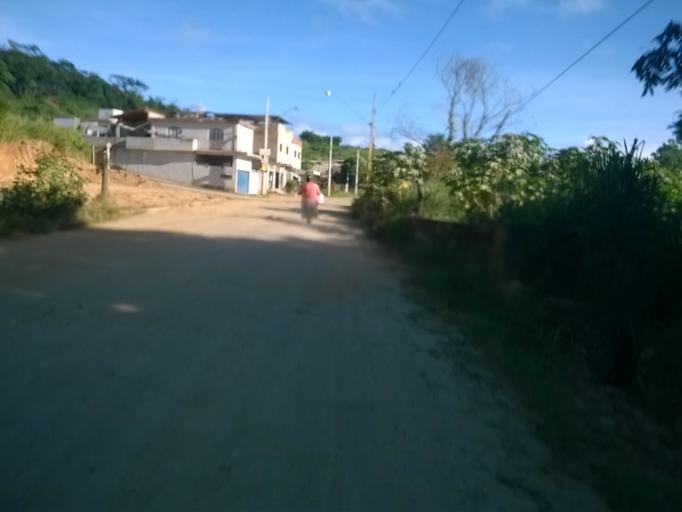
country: BR
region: Minas Gerais
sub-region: Uba
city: Uba
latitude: -21.0853
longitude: -42.9814
